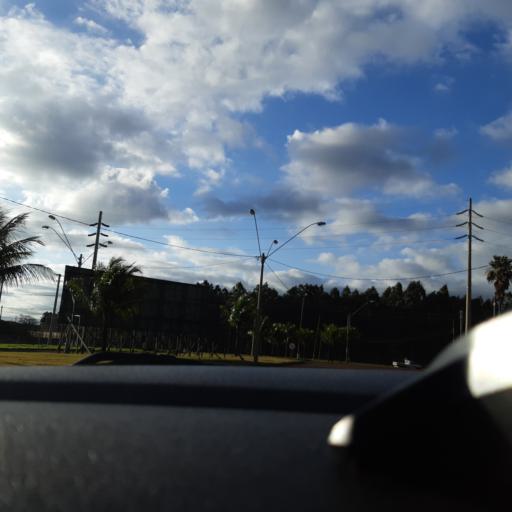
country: BR
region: Sao Paulo
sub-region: Ourinhos
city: Ourinhos
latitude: -22.9971
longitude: -49.8526
